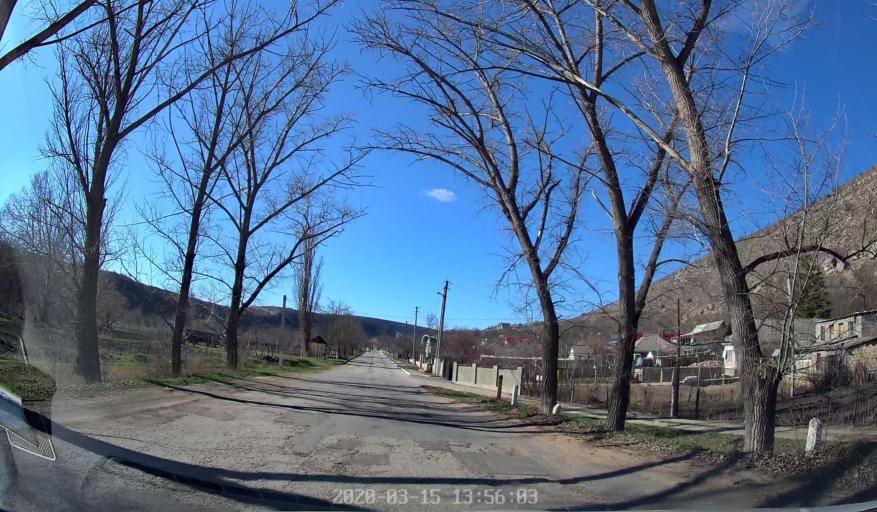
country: MD
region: Telenesti
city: Cocieri
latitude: 47.3094
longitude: 28.9885
